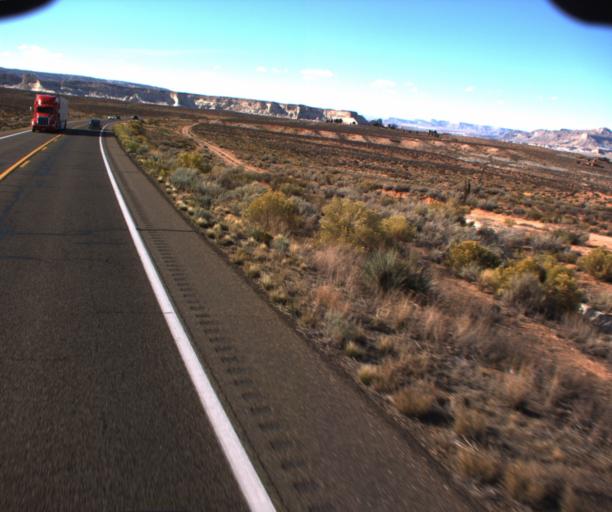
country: US
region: Arizona
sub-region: Coconino County
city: Page
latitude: 36.9828
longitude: -111.5481
